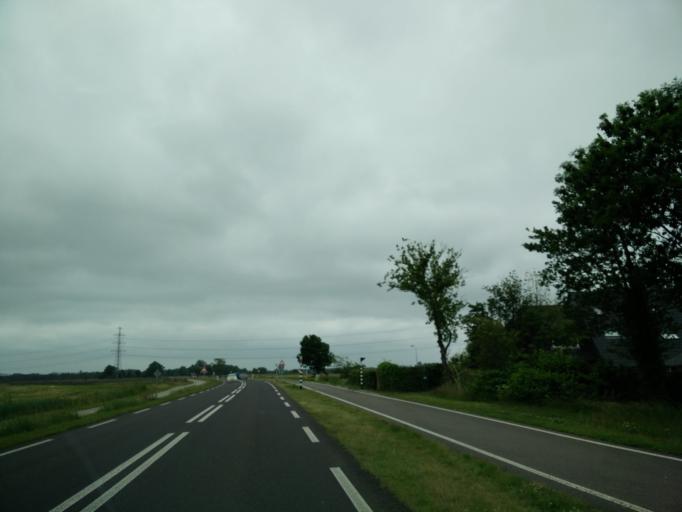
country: NL
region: Groningen
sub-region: Gemeente Groningen
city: Groningen
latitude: 53.1791
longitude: 6.5039
